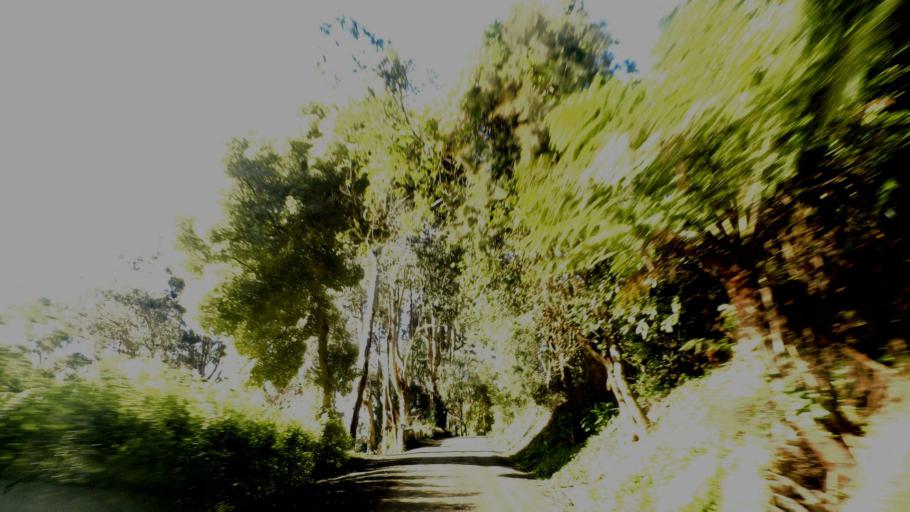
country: AU
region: Victoria
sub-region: Yarra Ranges
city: Mount Dandenong
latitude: -37.8266
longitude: 145.3678
